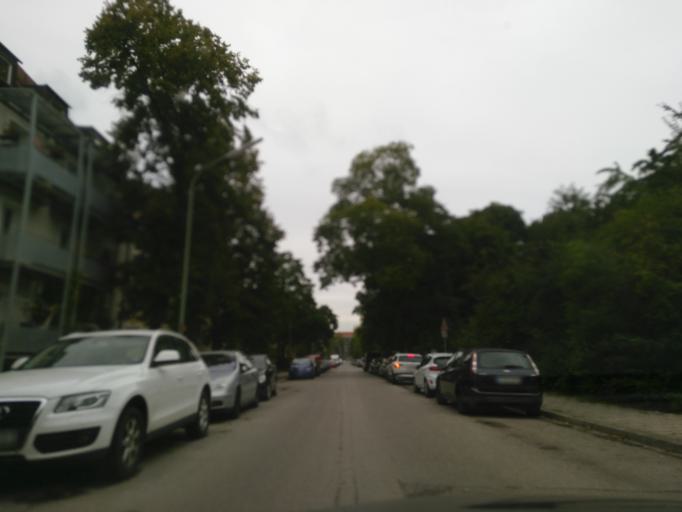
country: DE
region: Bavaria
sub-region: Upper Bavaria
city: Munich
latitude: 48.1031
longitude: 11.5946
